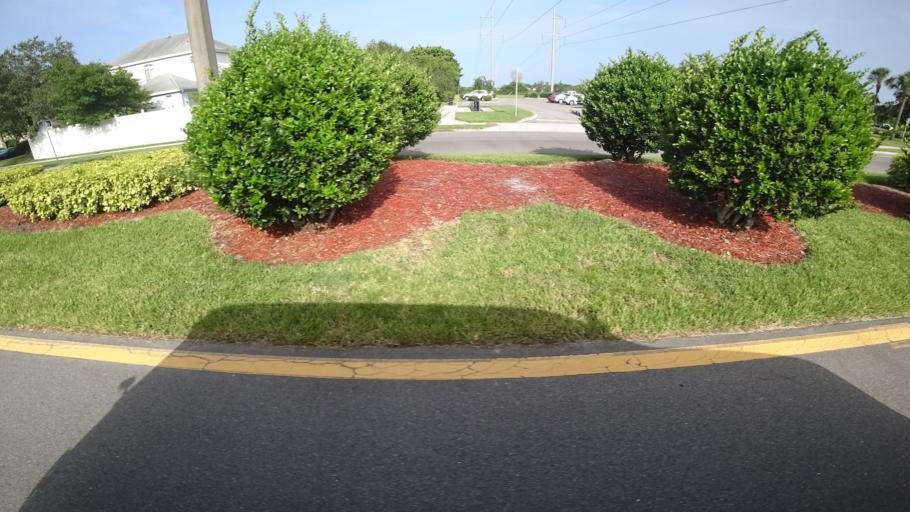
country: US
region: Florida
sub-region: Manatee County
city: Ellenton
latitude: 27.5518
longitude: -82.4995
